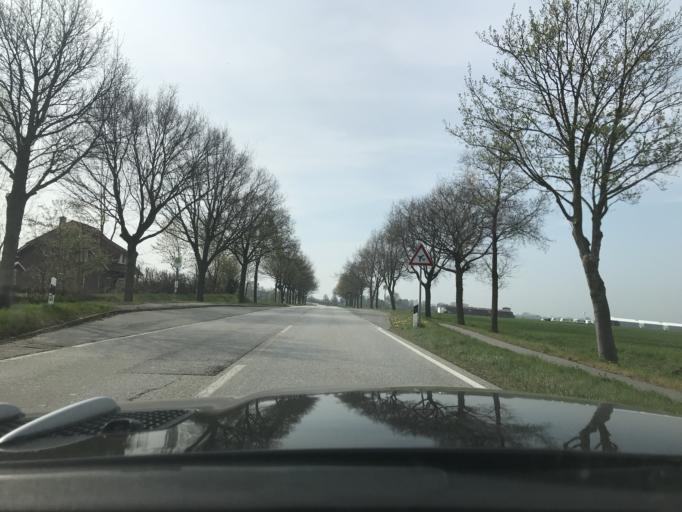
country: DE
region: Schleswig-Holstein
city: Grube
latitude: 54.2478
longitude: 11.0310
